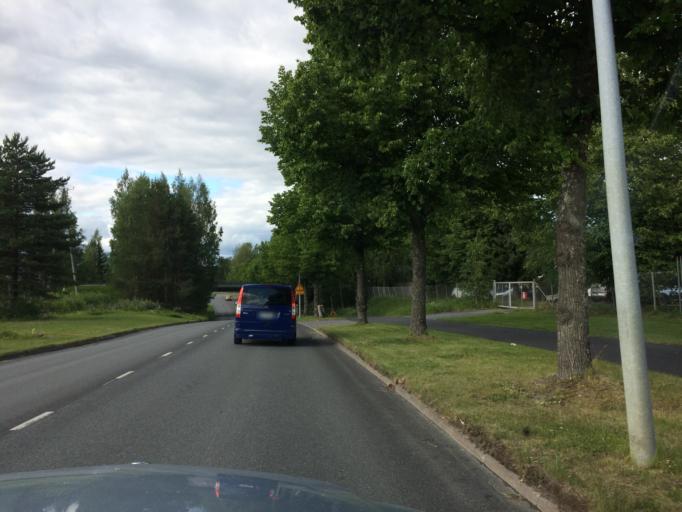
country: FI
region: Haeme
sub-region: Haemeenlinna
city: Parola
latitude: 61.0111
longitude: 24.3989
